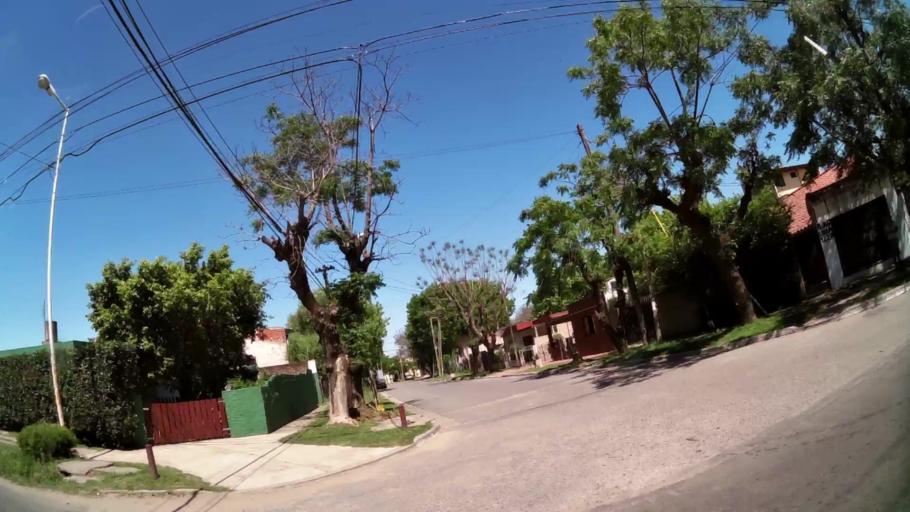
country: AR
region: Buenos Aires
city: Hurlingham
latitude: -34.4987
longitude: -58.6622
